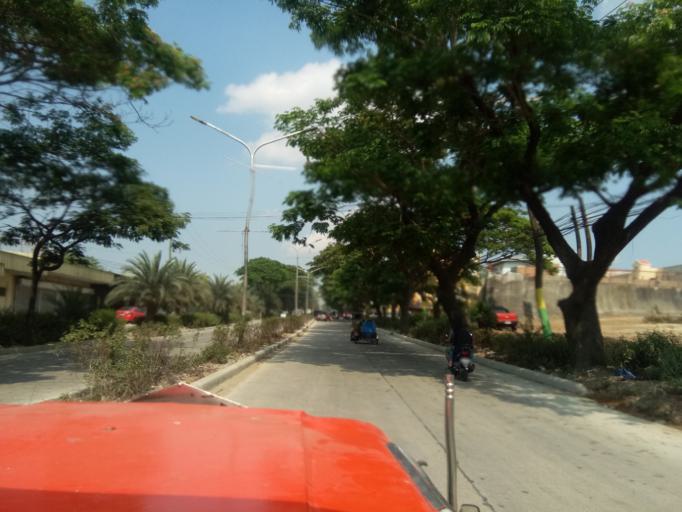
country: PH
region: Calabarzon
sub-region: Province of Cavite
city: Dasmarinas
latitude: 14.3268
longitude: 120.9471
